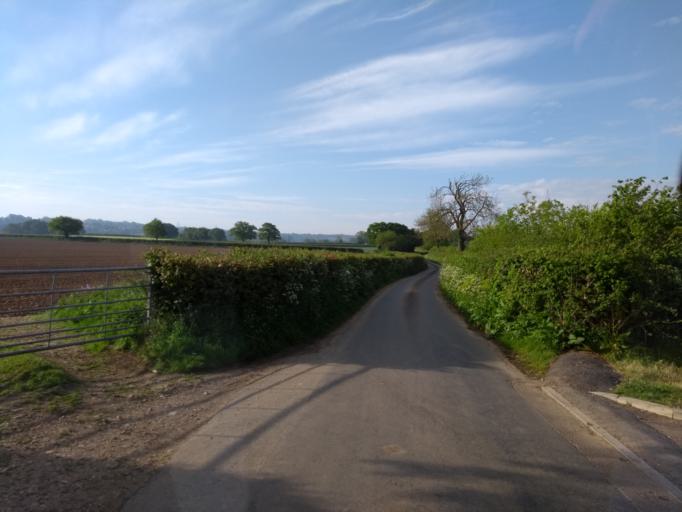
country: GB
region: England
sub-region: Devon
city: Axminster
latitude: 50.8131
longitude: -2.9523
